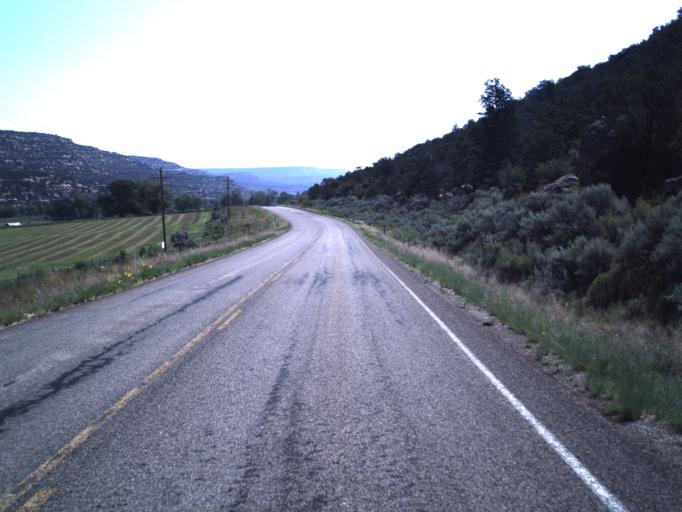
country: US
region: Utah
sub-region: Duchesne County
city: Duchesne
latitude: 40.2962
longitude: -110.5883
